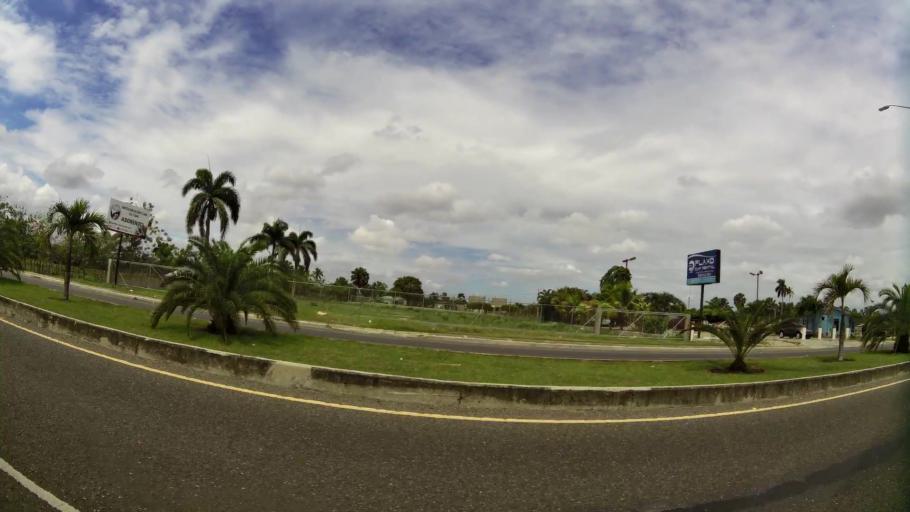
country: DO
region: Santiago
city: Licey al Medio
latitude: 19.3973
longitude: -70.6032
